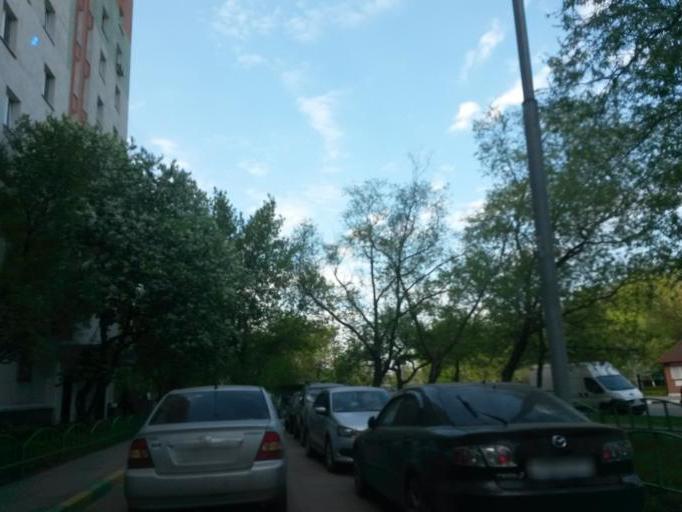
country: RU
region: Moscow
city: Mar'ino
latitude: 55.6532
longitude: 37.7112
